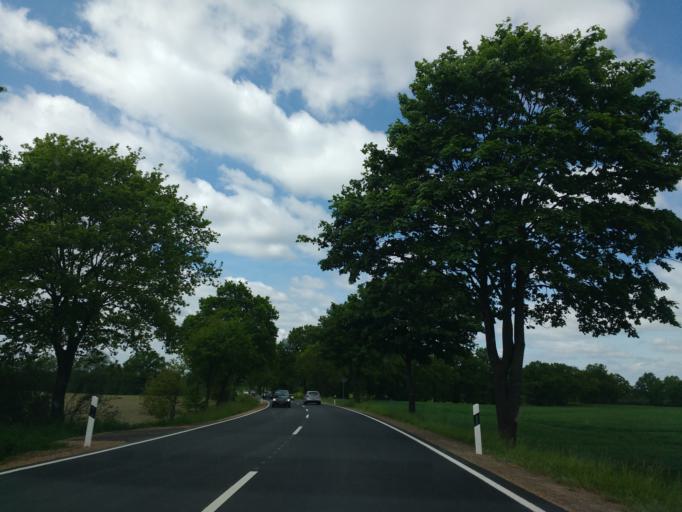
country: DE
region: Schleswig-Holstein
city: Braak
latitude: 53.5951
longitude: 10.2507
